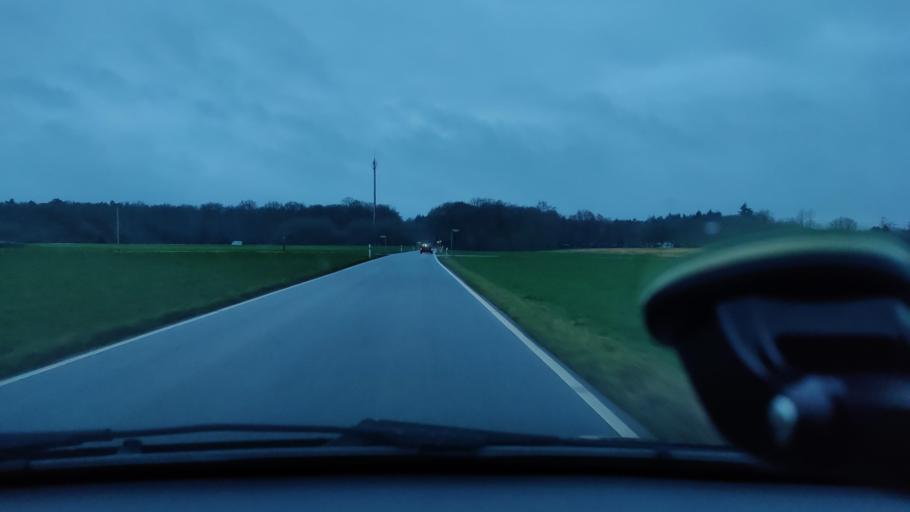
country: DE
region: North Rhine-Westphalia
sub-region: Regierungsbezirk Dusseldorf
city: Xanten
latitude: 51.6615
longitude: 6.4020
